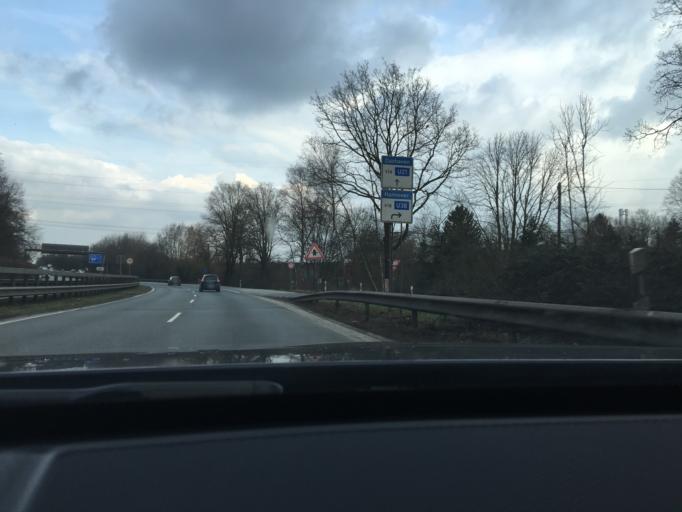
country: DE
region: Bremen
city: Bremen
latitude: 53.1125
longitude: 8.8106
